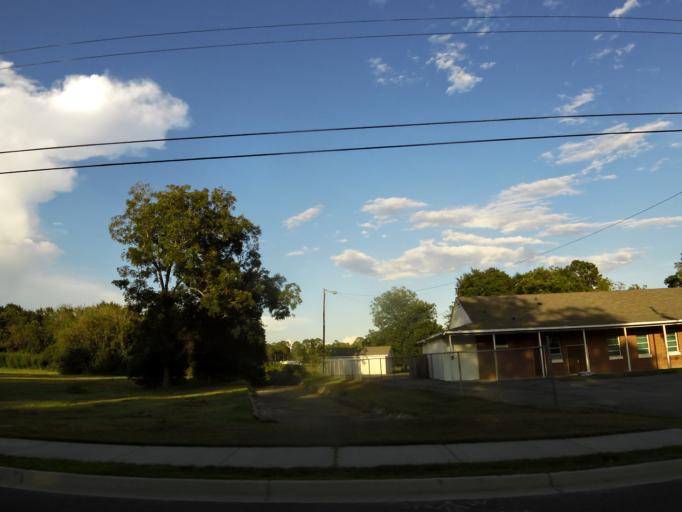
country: US
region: Georgia
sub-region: Lowndes County
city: Valdosta
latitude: 30.8220
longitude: -83.2695
